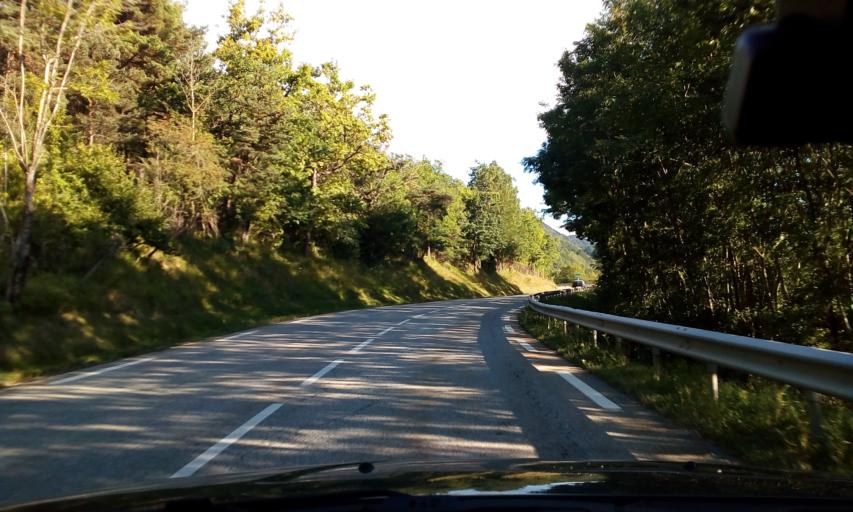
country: FR
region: Rhone-Alpes
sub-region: Departement de l'Isere
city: Le Gua
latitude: 44.9594
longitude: 5.6373
